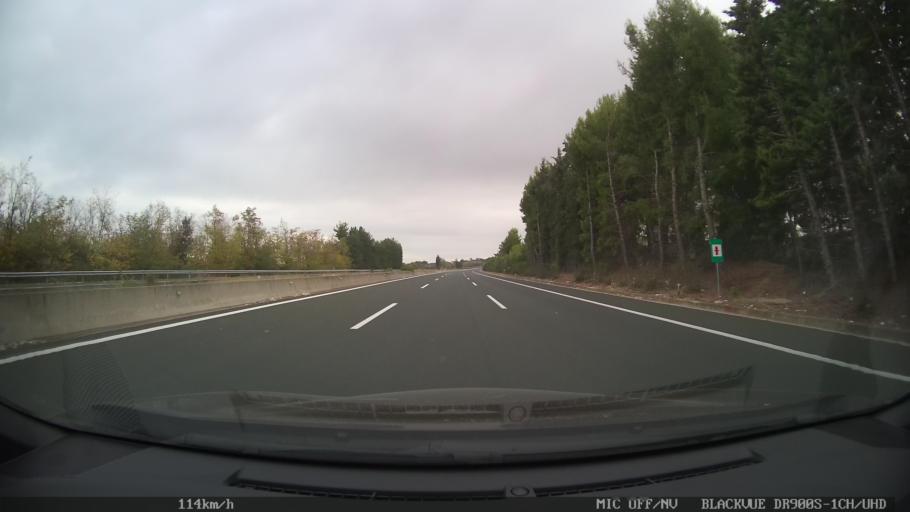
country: GR
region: Central Macedonia
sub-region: Nomos Pierias
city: Makrygialos
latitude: 40.3929
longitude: 22.6036
